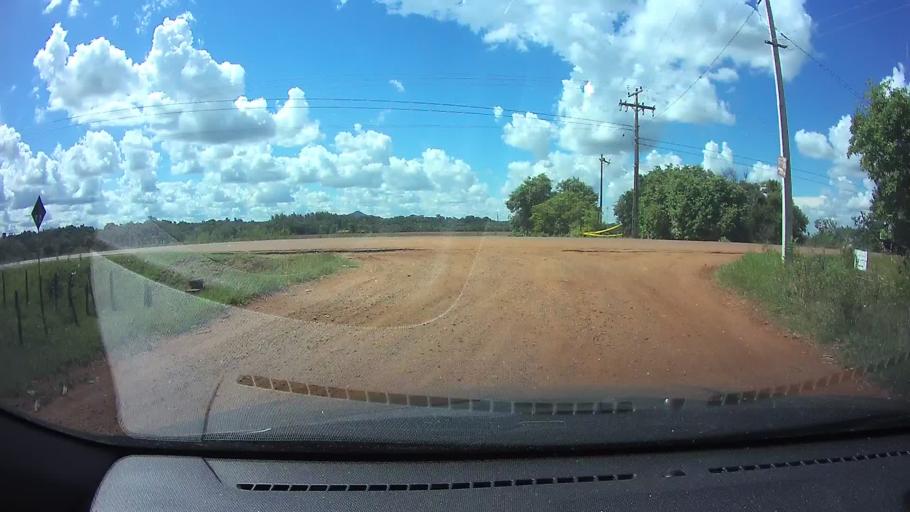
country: PY
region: Paraguari
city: La Colmena
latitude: -25.8985
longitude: -56.7925
